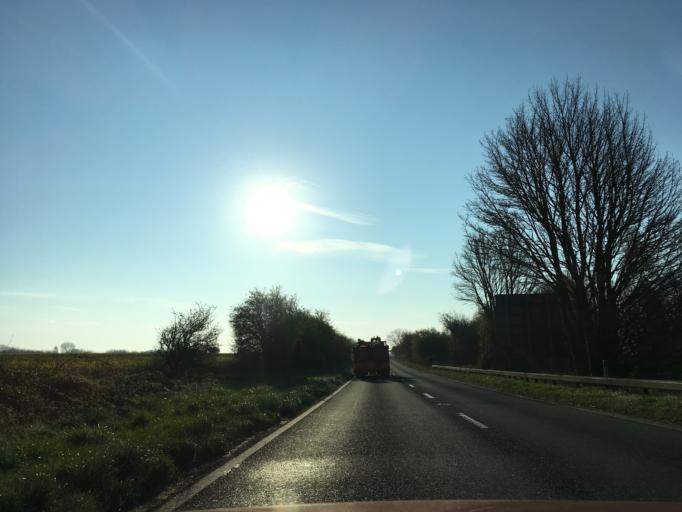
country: GB
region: England
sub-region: Oxfordshire
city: Burford
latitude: 51.8073
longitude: -1.6595
